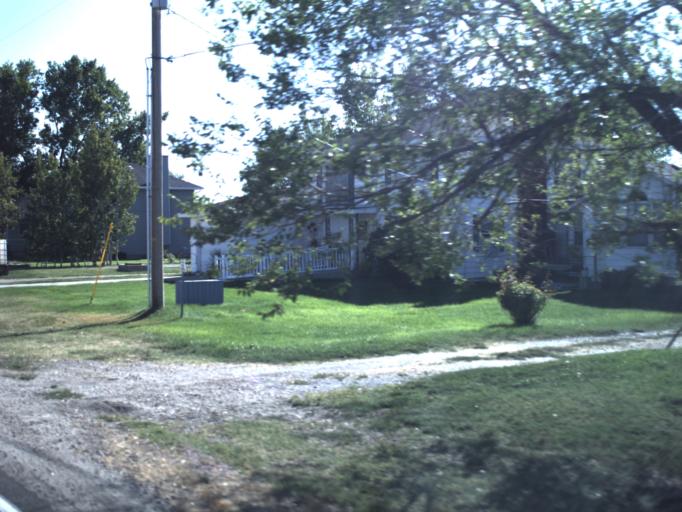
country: US
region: Utah
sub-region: Weber County
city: Hooper
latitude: 41.1849
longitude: -112.1227
